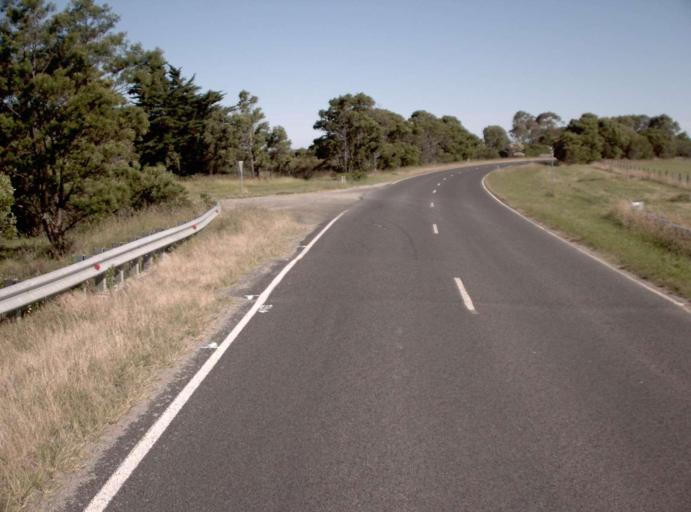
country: AU
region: Victoria
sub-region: Latrobe
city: Traralgon
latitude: -38.6276
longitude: 146.6762
